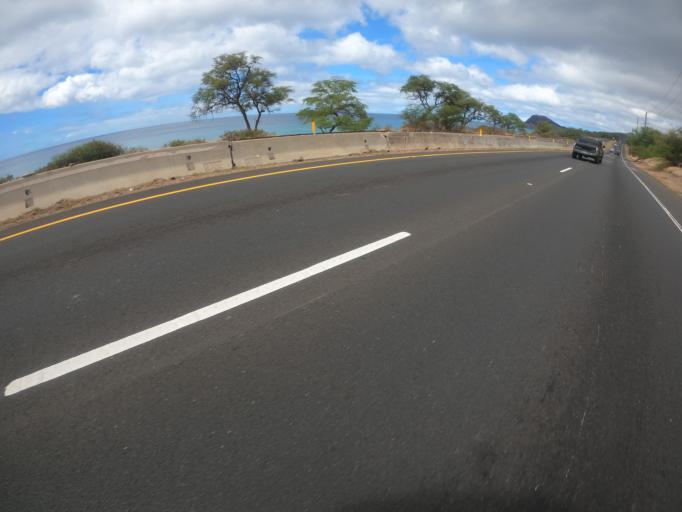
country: US
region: Hawaii
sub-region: Honolulu County
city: Nanakuli
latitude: 21.3641
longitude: -158.1333
